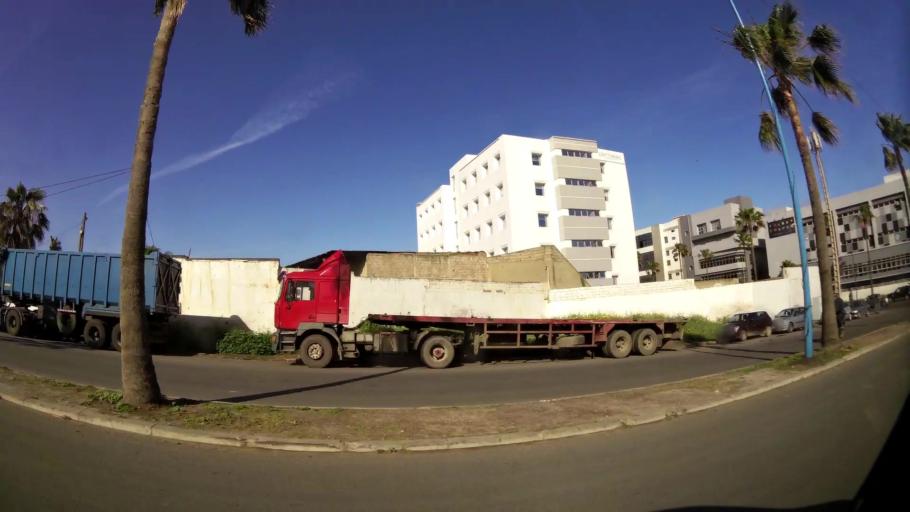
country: MA
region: Grand Casablanca
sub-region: Casablanca
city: Casablanca
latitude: 33.6053
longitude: -7.5749
